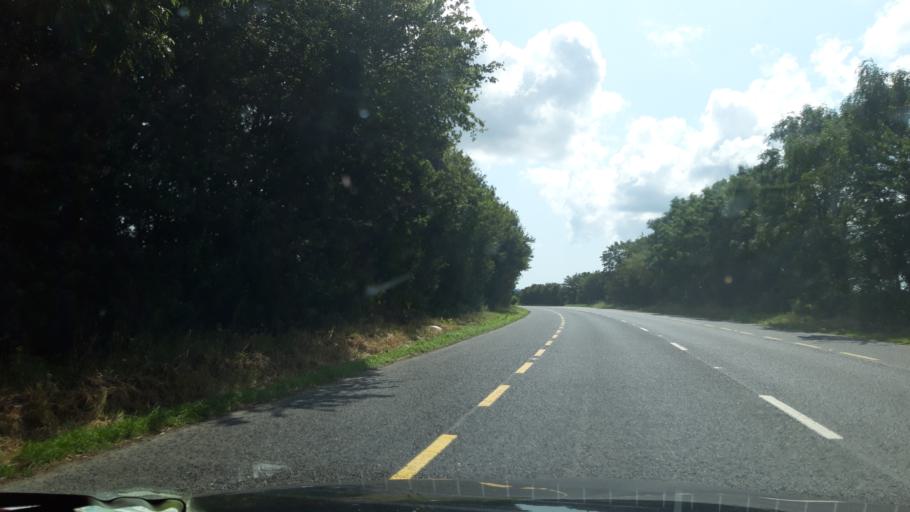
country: IE
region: Munster
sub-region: Waterford
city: Waterford
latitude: 52.2762
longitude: -7.0551
